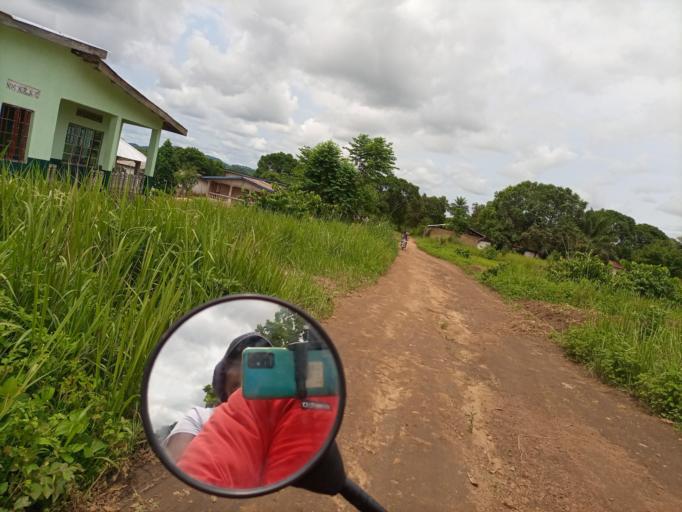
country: SL
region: Southern Province
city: Bo
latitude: 7.9684
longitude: -11.7153
